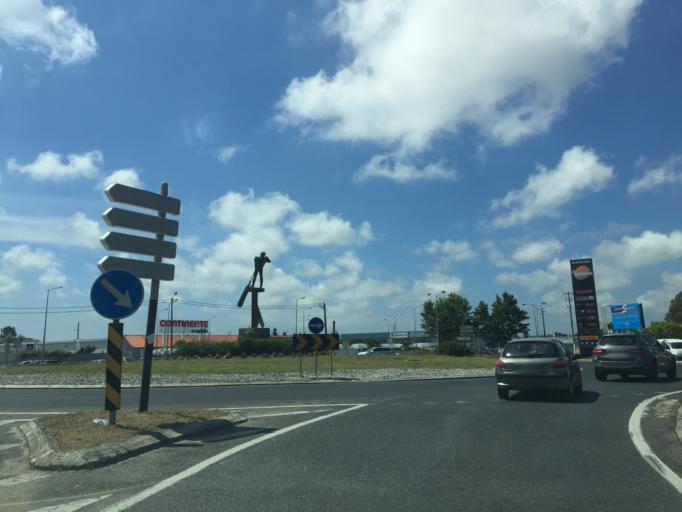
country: PT
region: Leiria
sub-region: Marinha Grande
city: Marinha Grande
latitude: 39.7344
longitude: -8.9320
